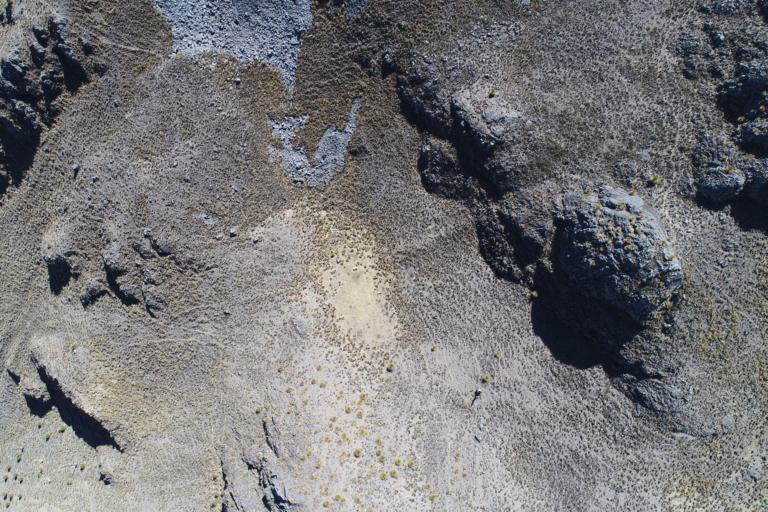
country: BO
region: La Paz
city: Viloco
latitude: -16.8087
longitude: -67.5463
